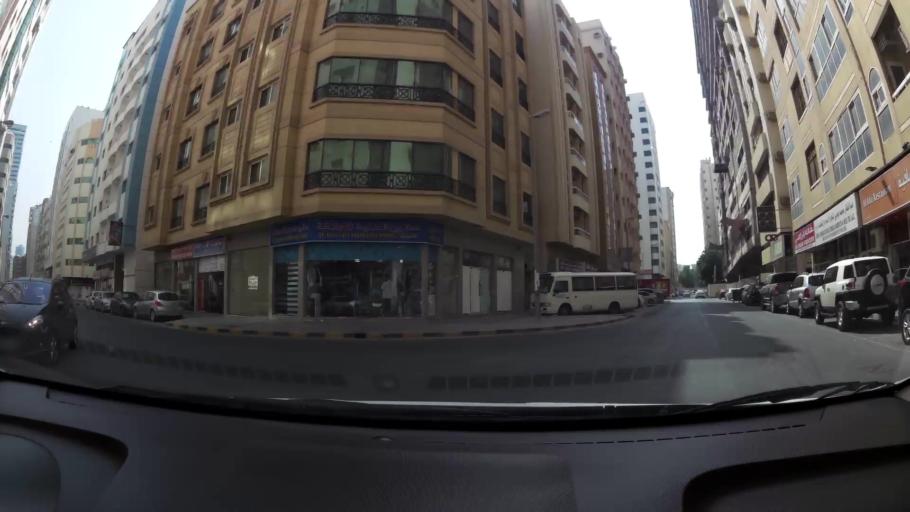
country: AE
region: Ash Shariqah
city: Sharjah
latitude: 25.3494
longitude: 55.3944
